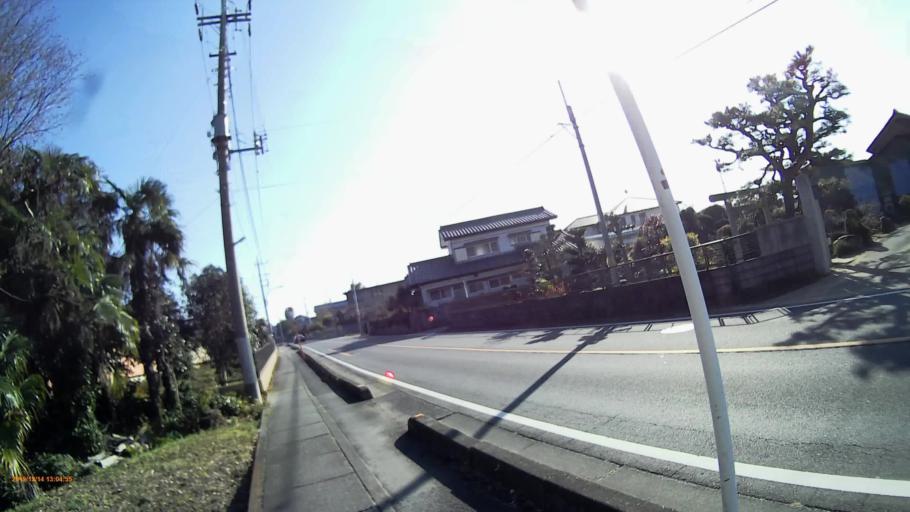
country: JP
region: Saitama
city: Fukiage-fujimi
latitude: 36.0931
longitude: 139.4647
